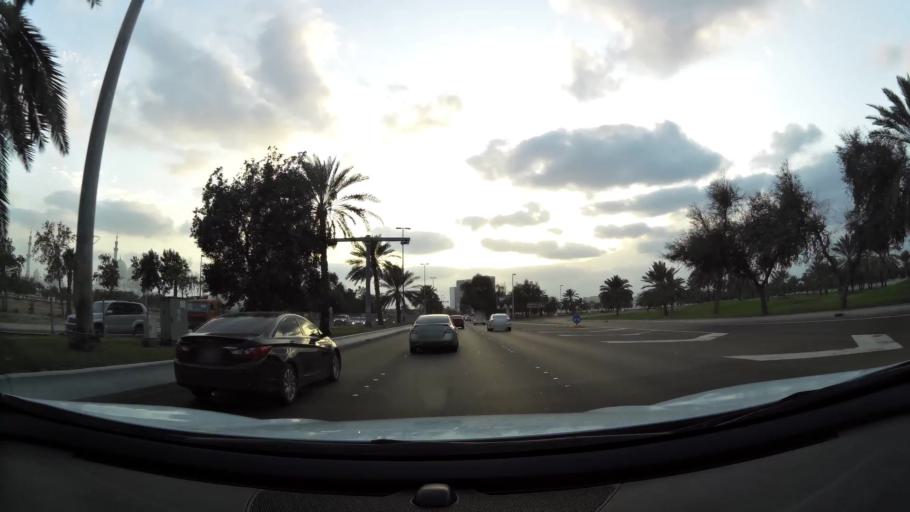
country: AE
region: Abu Dhabi
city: Abu Dhabi
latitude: 24.4192
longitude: 54.4770
